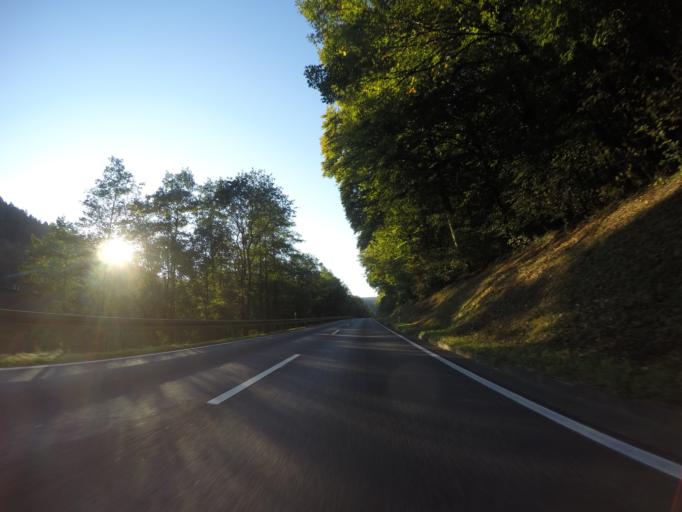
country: DE
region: Bavaria
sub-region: Regierungsbezirk Unterfranken
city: Hasloch
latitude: 49.8115
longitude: 9.4942
